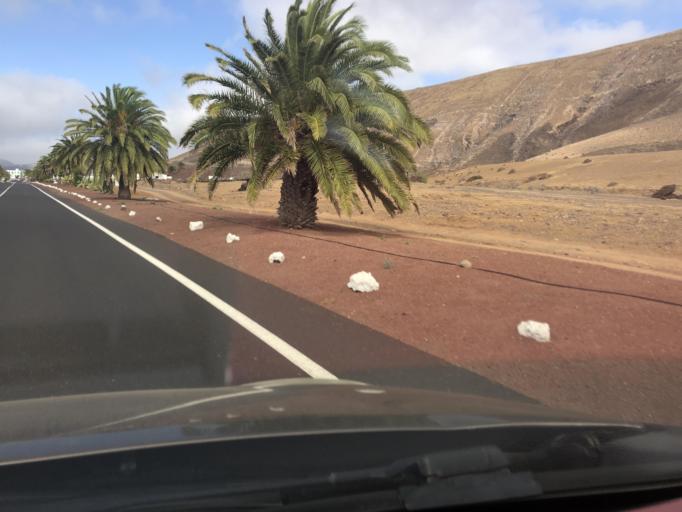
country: ES
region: Canary Islands
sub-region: Provincia de Las Palmas
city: Yaiza
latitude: 28.9520
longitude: -13.7795
